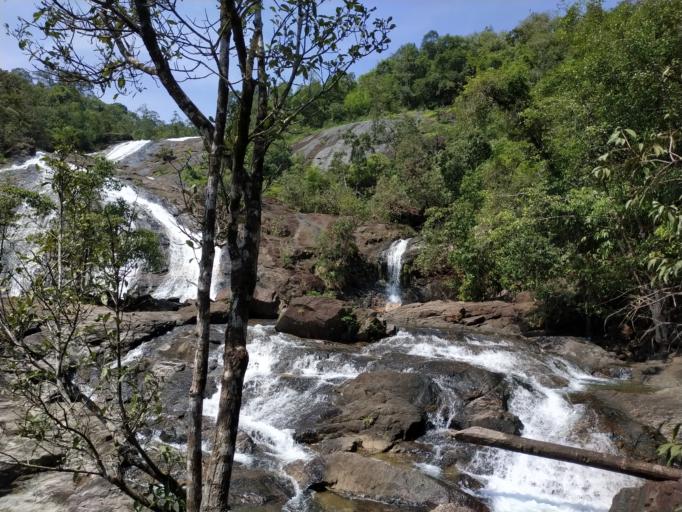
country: MM
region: Tanintharyi
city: Dawei
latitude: 14.5838
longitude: 98.0486
